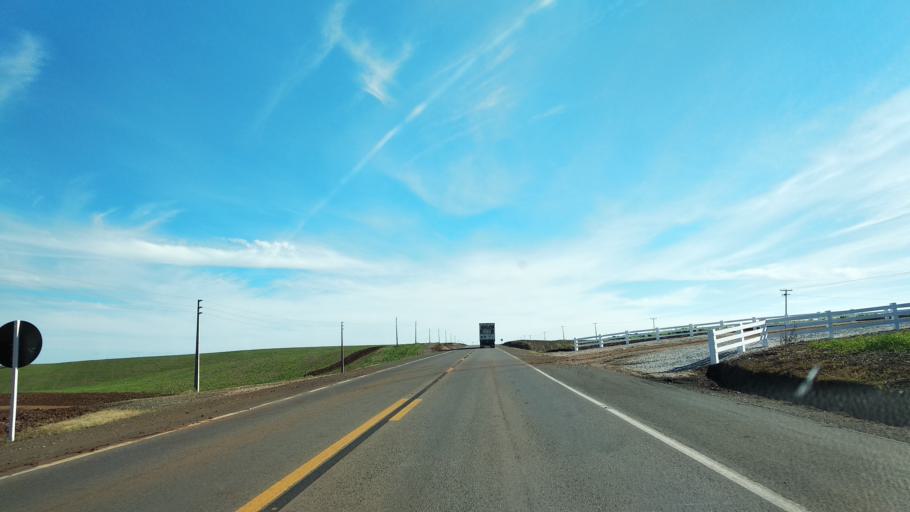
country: BR
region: Santa Catarina
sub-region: Campos Novos
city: Campos Novos
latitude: -27.4870
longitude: -51.3204
